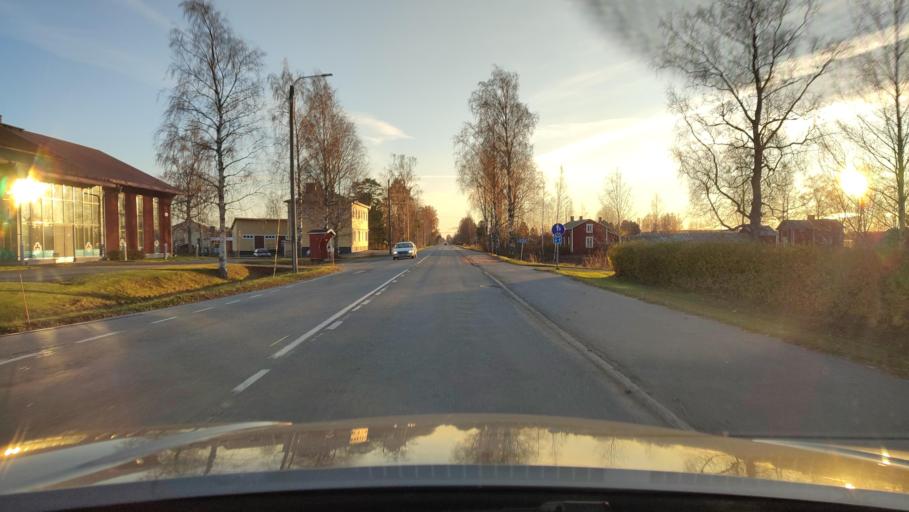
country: FI
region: Ostrobothnia
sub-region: Sydosterbotten
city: Naerpes
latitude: 62.5439
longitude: 21.3954
